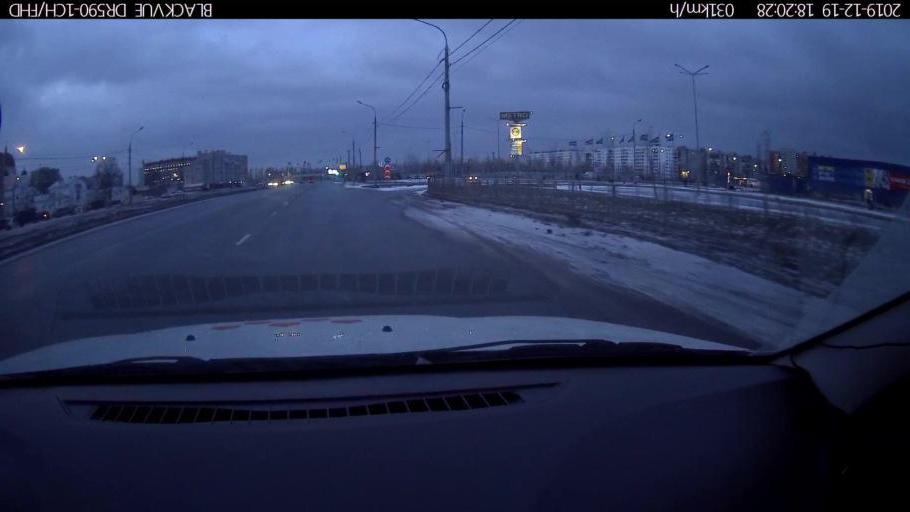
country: RU
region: Nizjnij Novgorod
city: Nizhniy Novgorod
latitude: 56.3333
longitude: 43.9536
